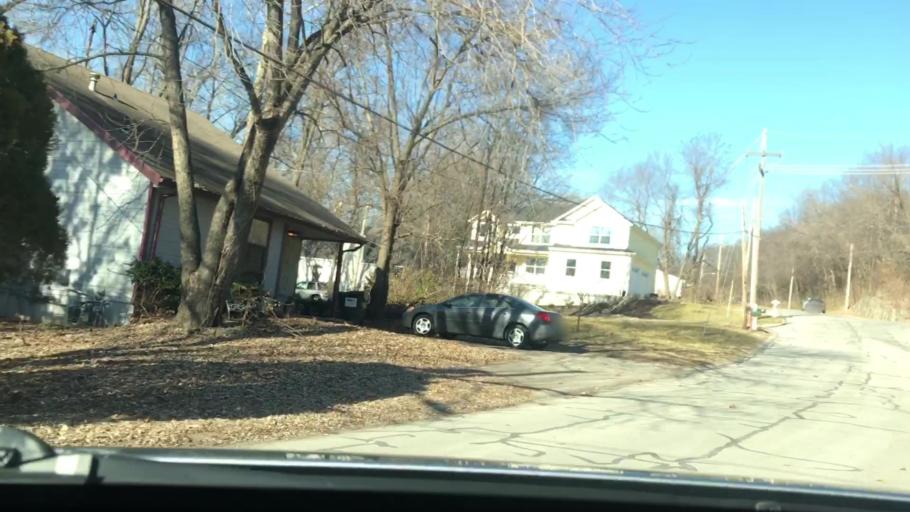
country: US
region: Missouri
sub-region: Platte County
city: Parkville
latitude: 39.1956
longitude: -94.6842
